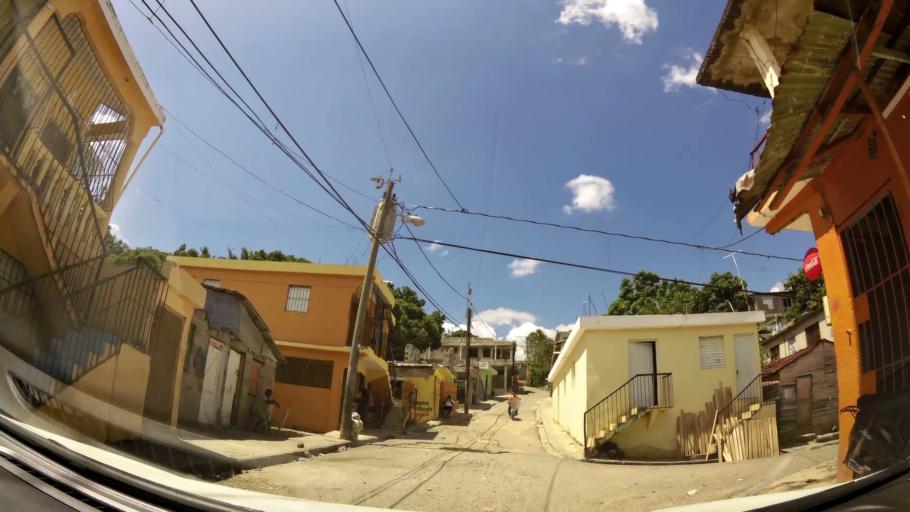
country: DO
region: San Cristobal
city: San Cristobal
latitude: 18.4049
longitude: -70.1154
